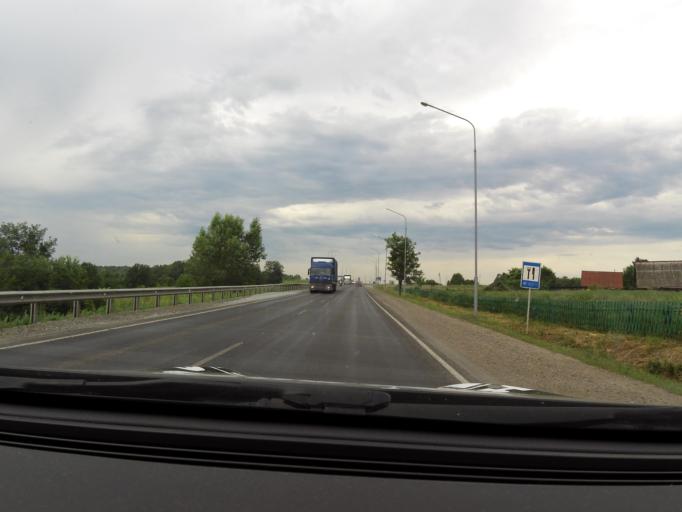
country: RU
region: Bashkortostan
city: Urman
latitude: 54.8219
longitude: 56.8841
